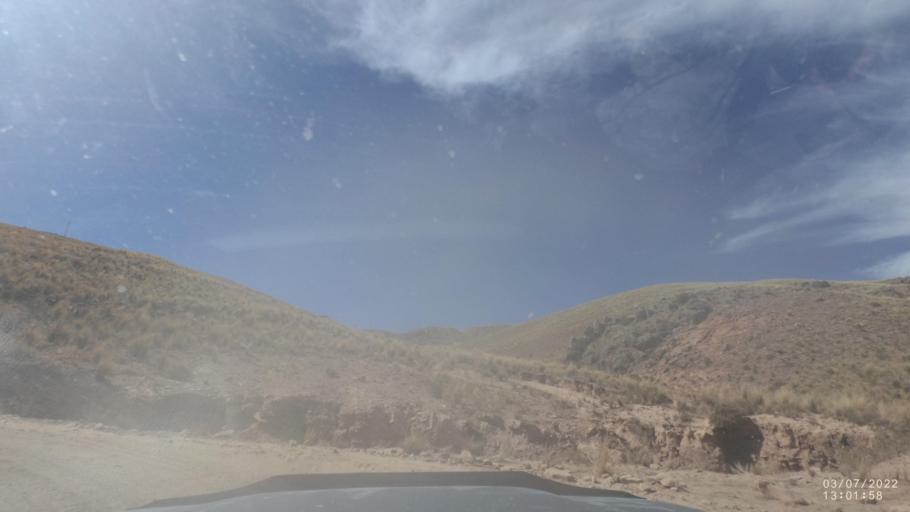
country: BO
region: Cochabamba
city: Colchani
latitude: -17.7076
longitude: -66.6907
